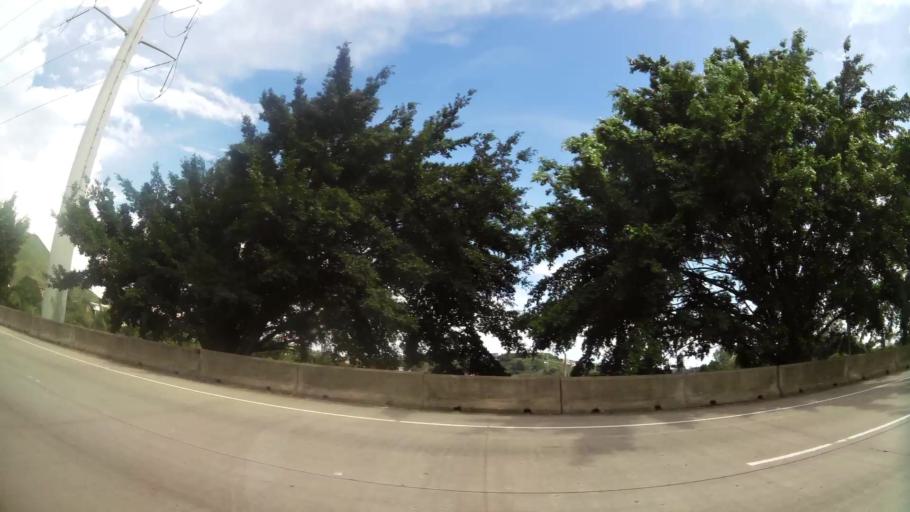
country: PA
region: Panama
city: Las Cumbres
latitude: 9.0430
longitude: -79.5296
